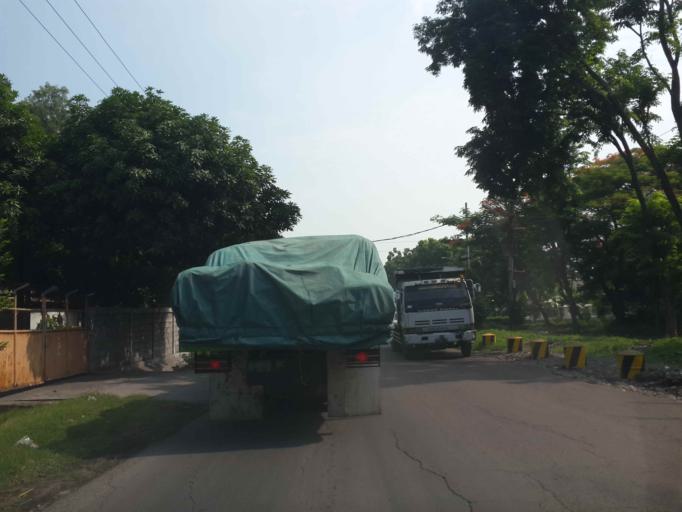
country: ID
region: East Java
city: Gresik
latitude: -7.1710
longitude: 112.6608
